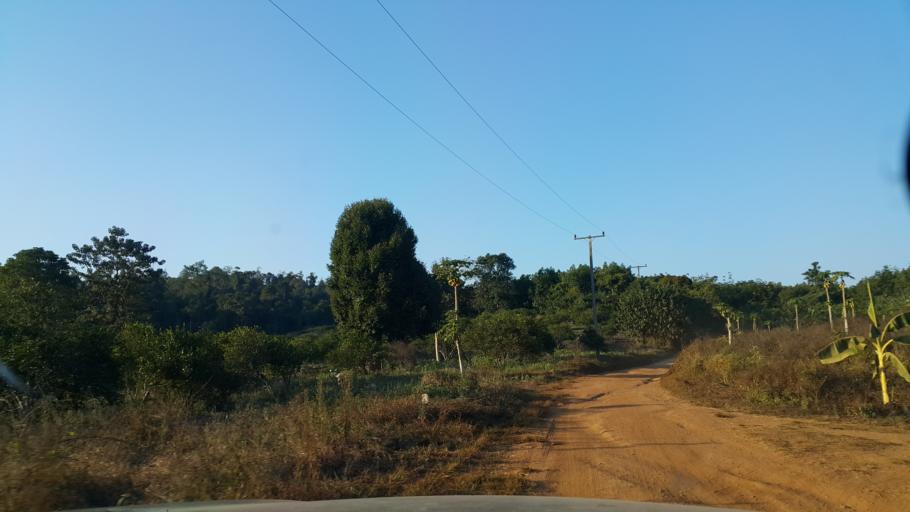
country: TH
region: Sukhothai
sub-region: Amphoe Si Satchanalai
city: Si Satchanalai
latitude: 17.5990
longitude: 99.6134
